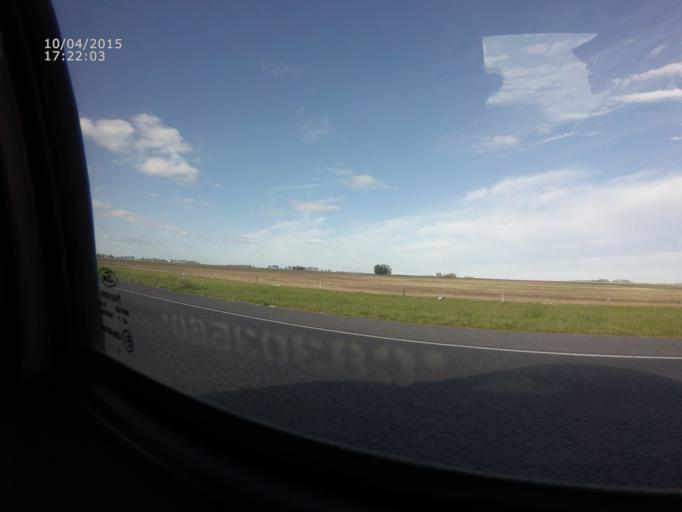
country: AR
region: Buenos Aires
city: Maipu
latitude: -37.1222
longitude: -57.8213
